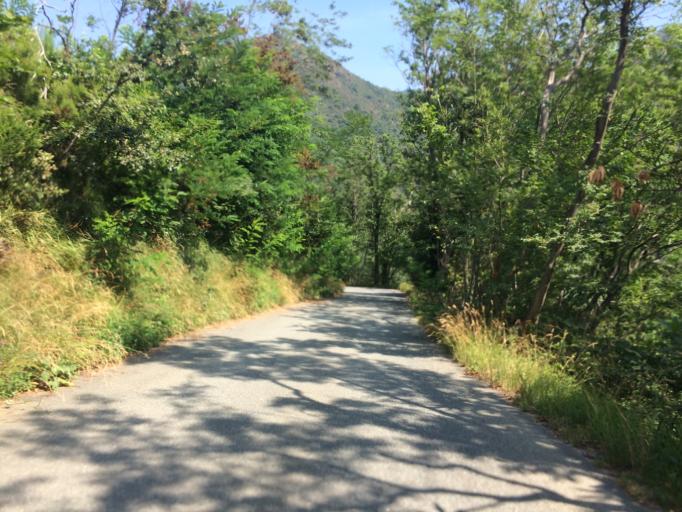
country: IT
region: Liguria
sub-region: Provincia di Genova
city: Sciarborasca
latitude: 44.4021
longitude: 8.5753
